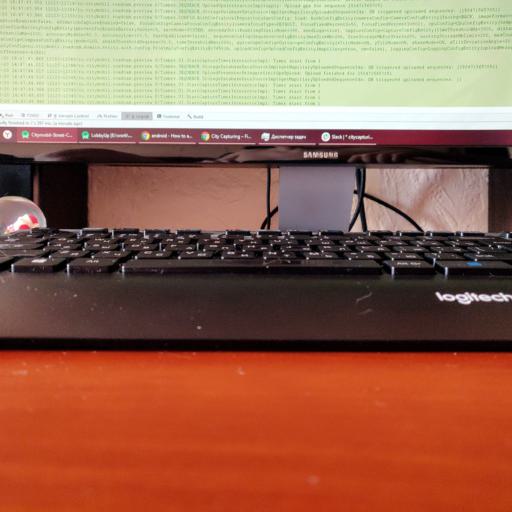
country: EE
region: Hiiumaa
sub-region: Kaerdla linn
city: Kardla
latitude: 59.1210
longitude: 22.8249
